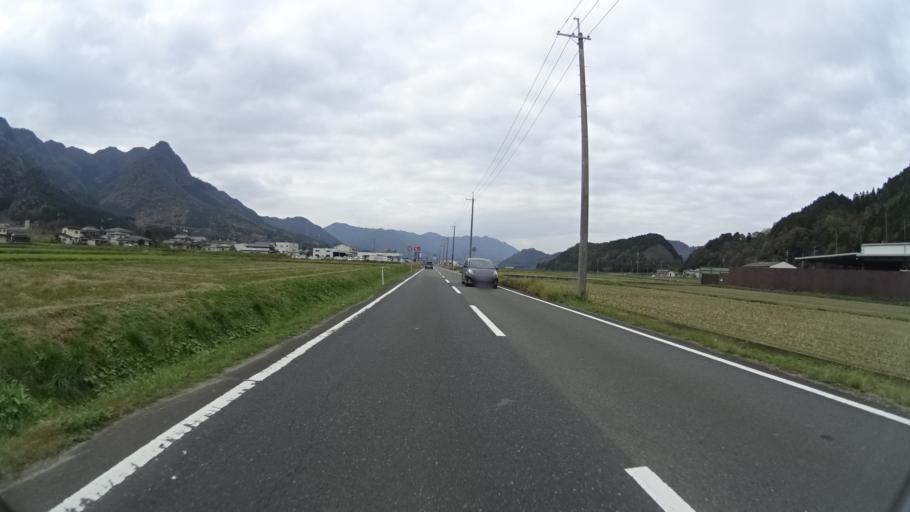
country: JP
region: Hyogo
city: Sasayama
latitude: 35.1427
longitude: 135.1672
